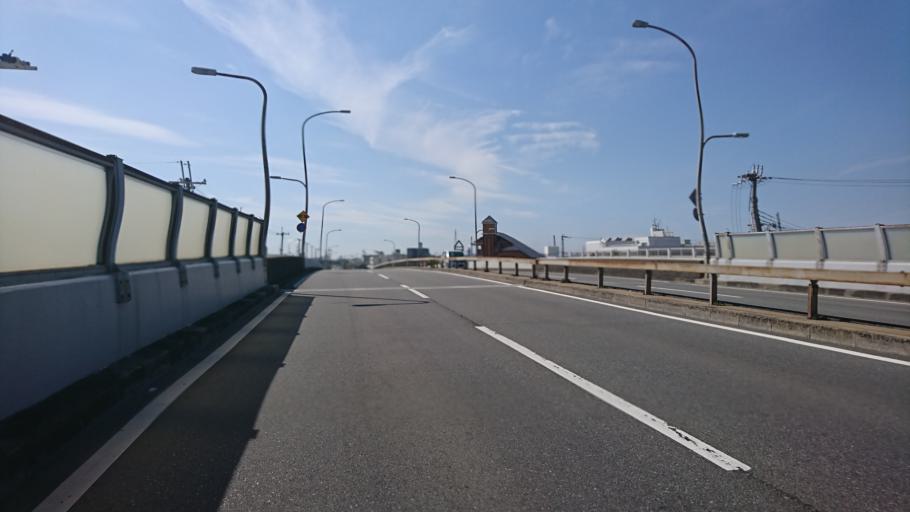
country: JP
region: Hyogo
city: Kakogawacho-honmachi
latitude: 34.7149
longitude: 134.8701
